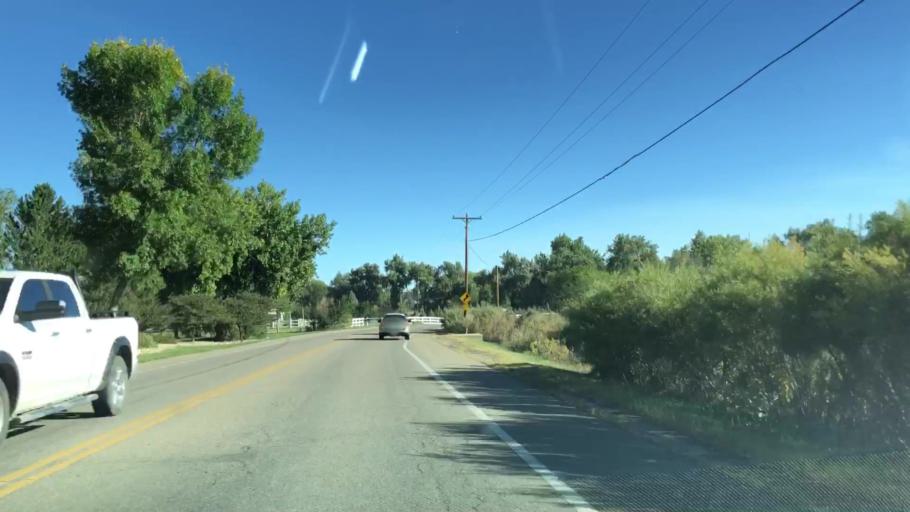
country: US
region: Colorado
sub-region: Larimer County
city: Loveland
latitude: 40.3974
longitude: -105.1249
